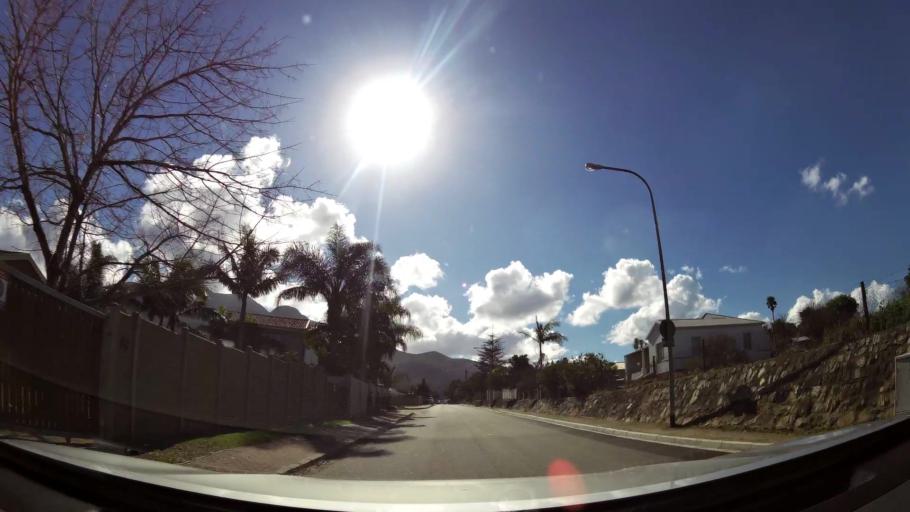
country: ZA
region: Western Cape
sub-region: Eden District Municipality
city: George
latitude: -33.9475
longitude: 22.4729
